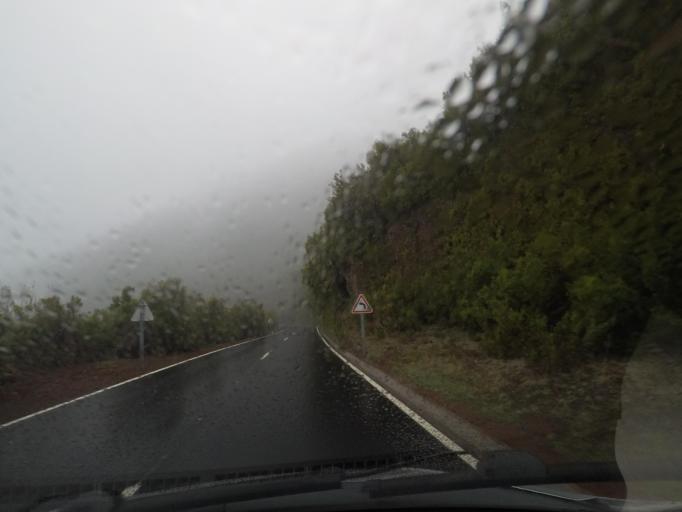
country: PT
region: Madeira
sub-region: Santana
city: Santana
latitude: 32.7693
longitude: -16.9169
